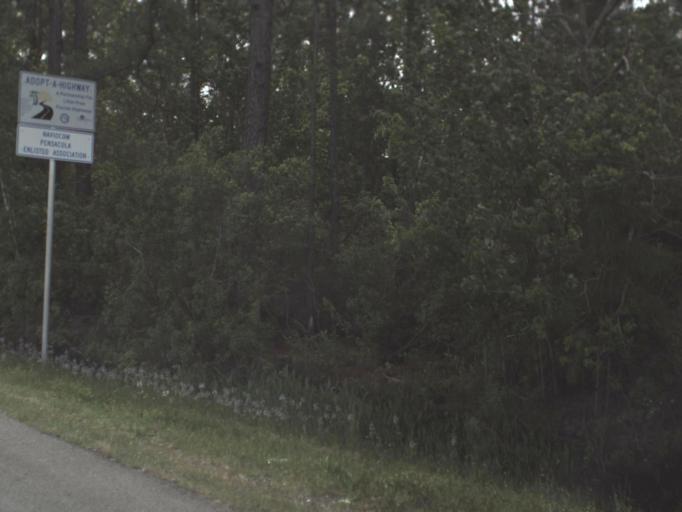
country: US
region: Florida
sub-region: Escambia County
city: Myrtle Grove
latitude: 30.4026
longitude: -87.3426
